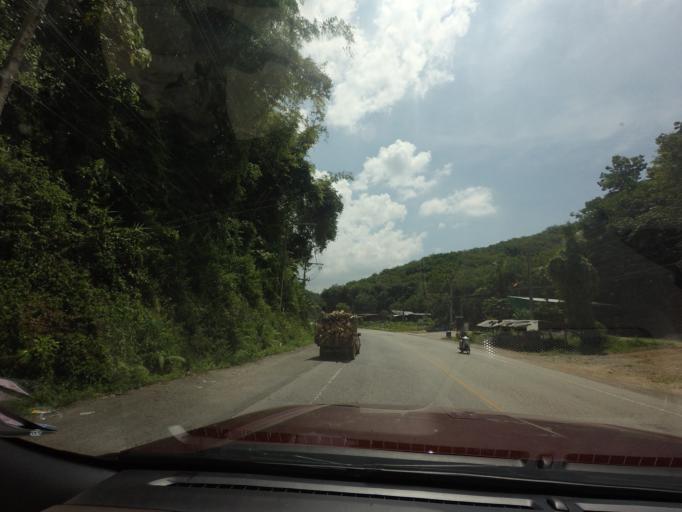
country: TH
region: Yala
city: Betong
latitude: 5.7973
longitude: 101.0710
